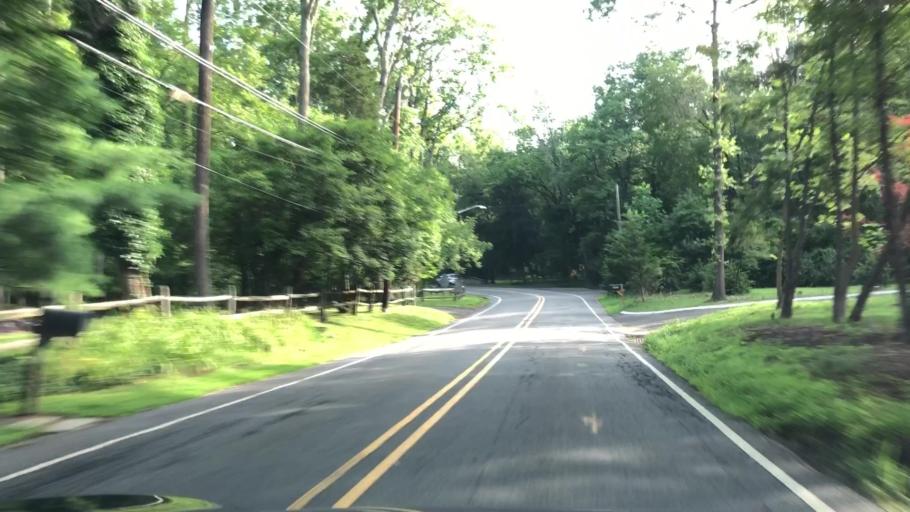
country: US
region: New Jersey
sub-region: Mercer County
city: Princeton
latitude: 40.3343
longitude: -74.7010
